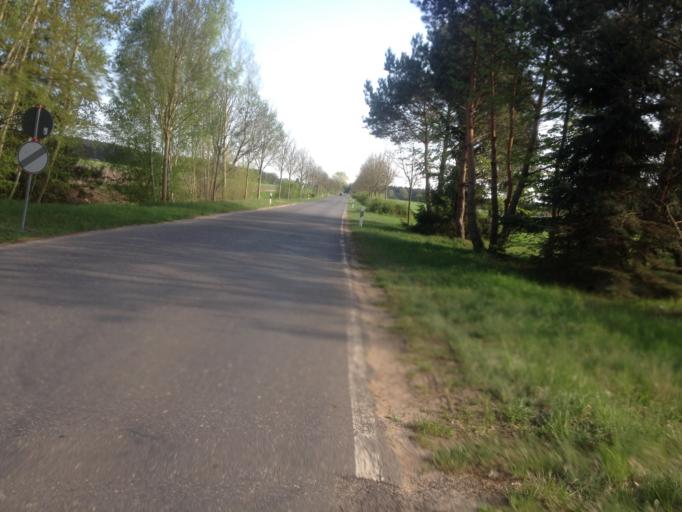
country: DE
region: Brandenburg
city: Drachhausen
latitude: 51.8857
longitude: 14.3128
